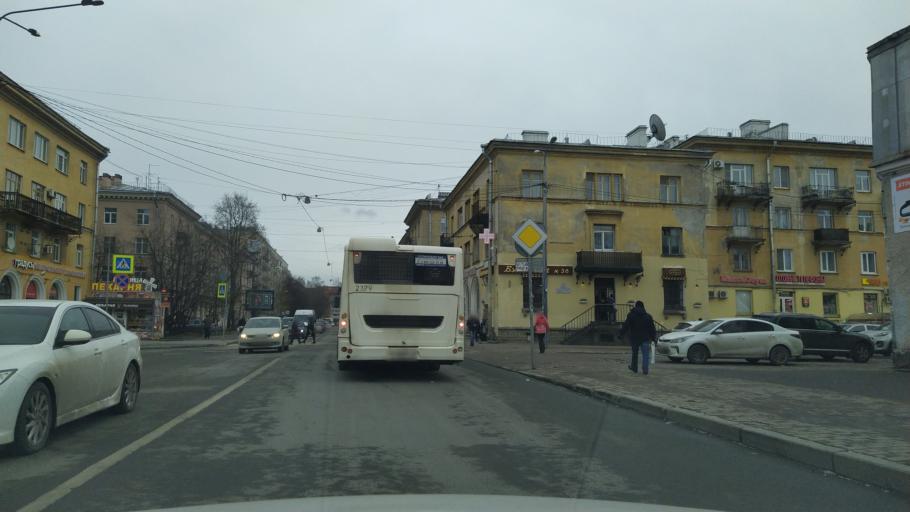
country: RU
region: Leningrad
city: Udel'naya
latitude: 60.0177
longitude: 30.3140
